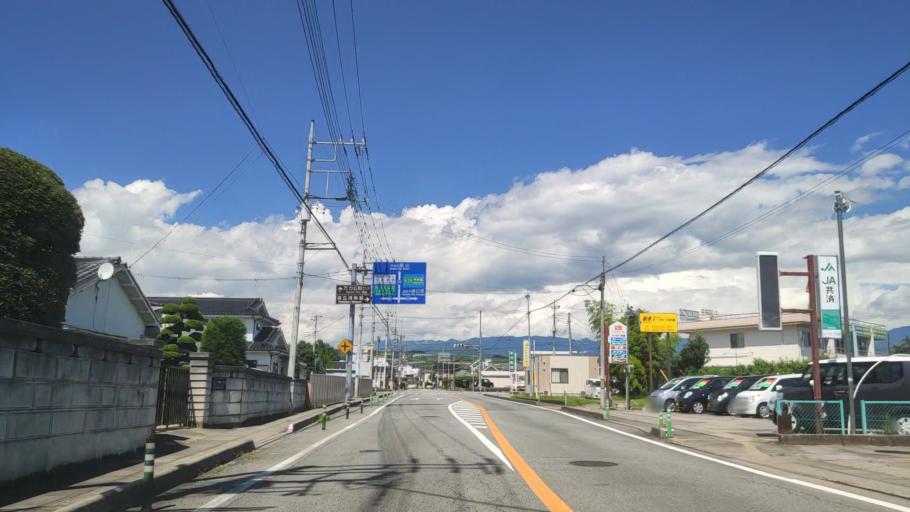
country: JP
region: Yamanashi
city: Isawa
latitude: 35.6802
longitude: 138.6602
